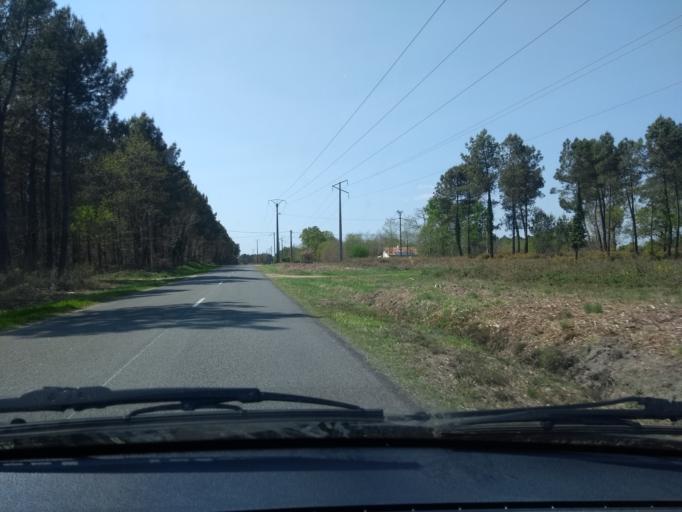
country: FR
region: Aquitaine
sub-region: Departement de la Gironde
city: Belin-Beliet
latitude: 44.5274
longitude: -0.7226
